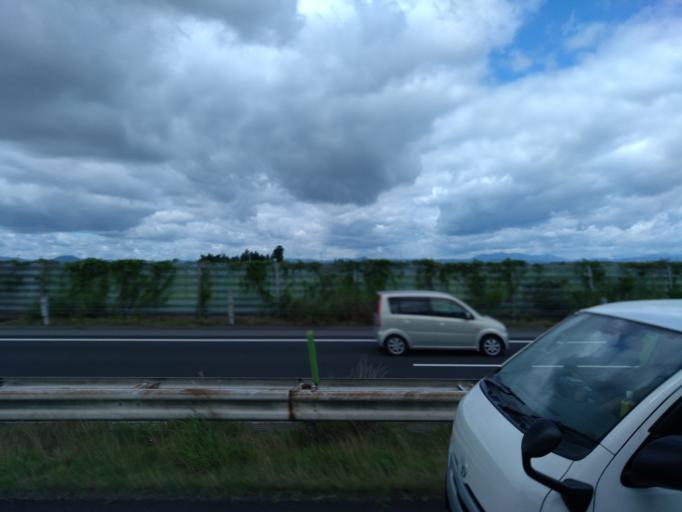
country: JP
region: Miyagi
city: Furukawa
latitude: 38.6082
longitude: 140.9426
